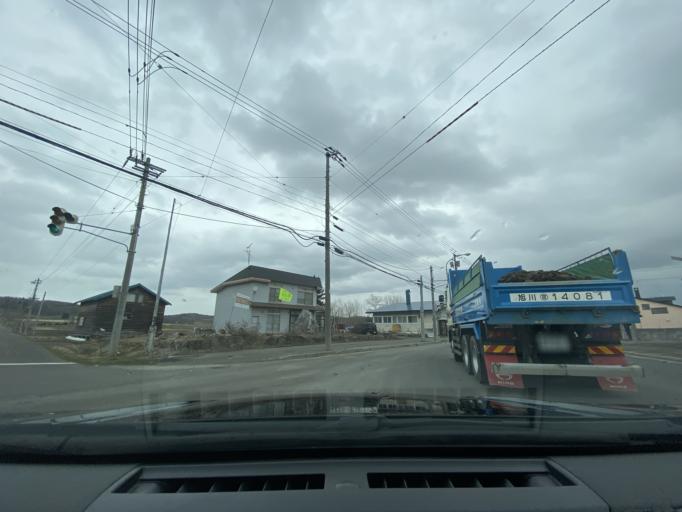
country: JP
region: Hokkaido
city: Nayoro
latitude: 44.1788
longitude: 142.2755
